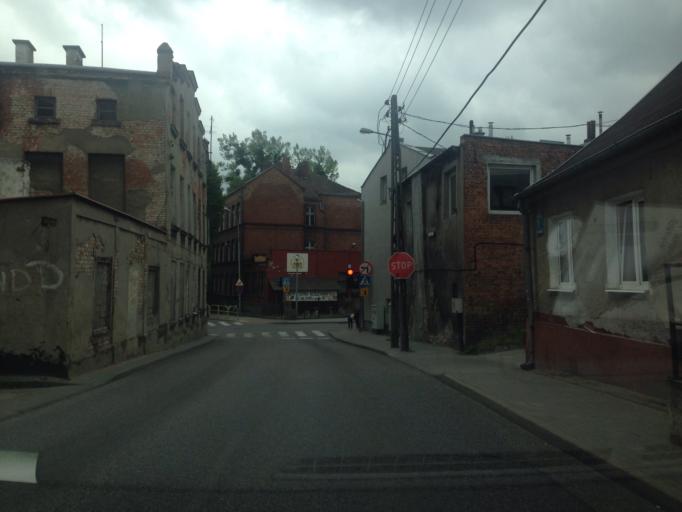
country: PL
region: Pomeranian Voivodeship
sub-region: Gdansk
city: Gdansk
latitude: 54.3306
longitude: 18.6306
